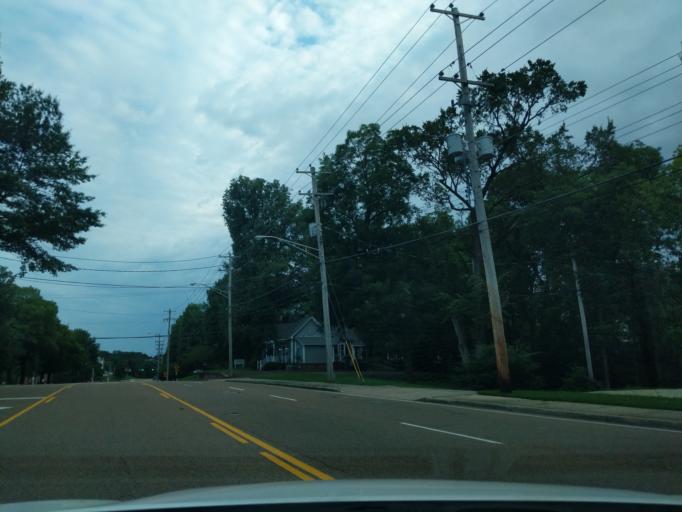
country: US
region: Tennessee
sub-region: Shelby County
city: Germantown
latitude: 35.0872
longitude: -89.8117
